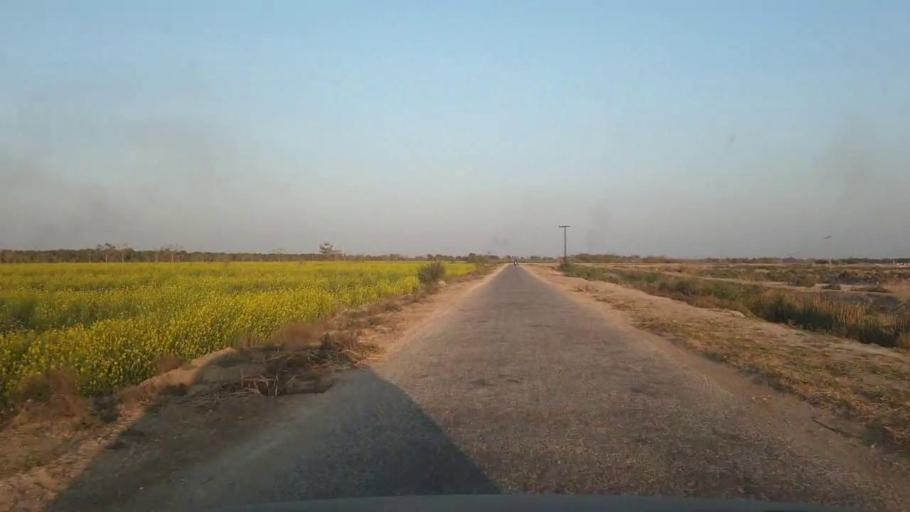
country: PK
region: Sindh
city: Mirwah Gorchani
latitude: 25.2789
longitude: 68.9365
